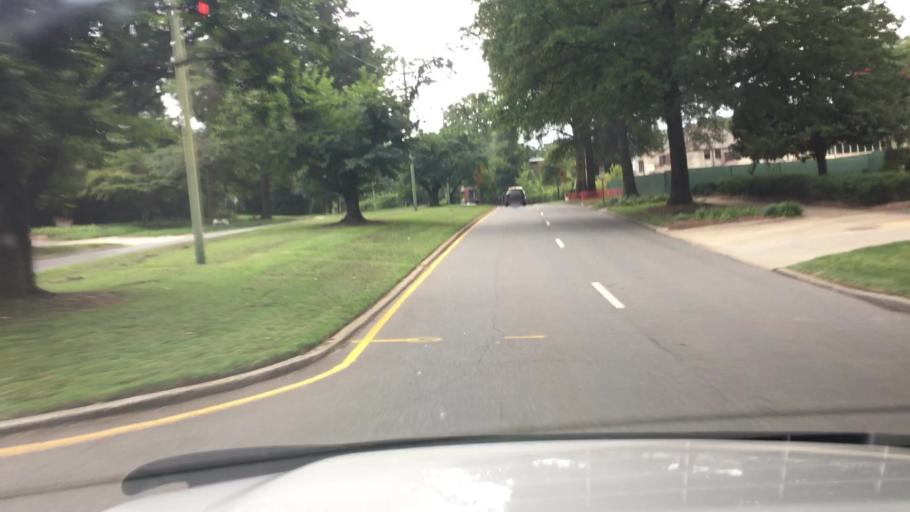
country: US
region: North Carolina
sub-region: Mecklenburg County
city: Charlotte
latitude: 35.1997
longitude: -80.8308
